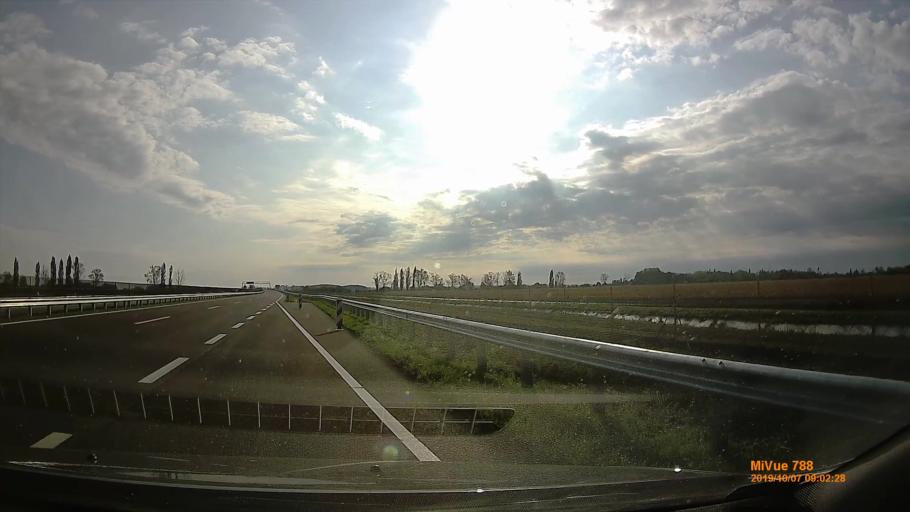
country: HU
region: Bekes
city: Szarvas
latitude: 46.8186
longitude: 20.5195
